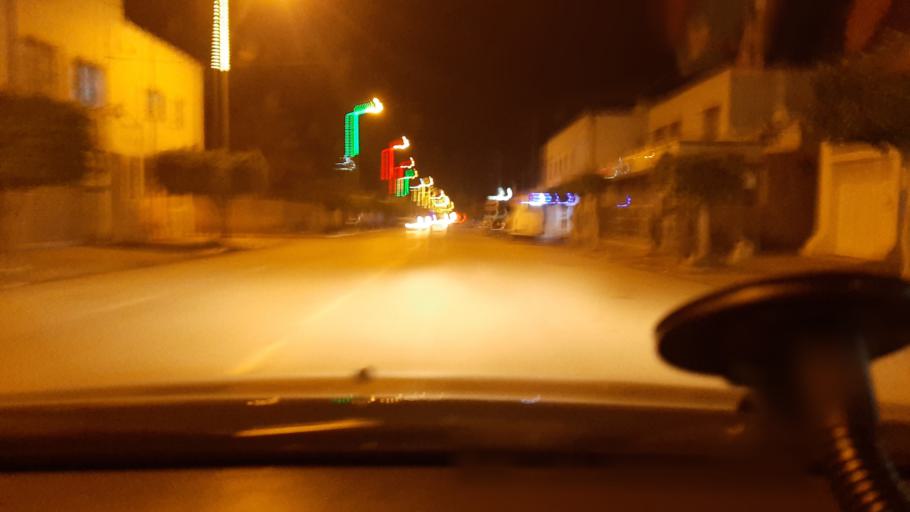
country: TN
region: Safaqis
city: Sfax
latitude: 34.7803
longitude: 10.7243
